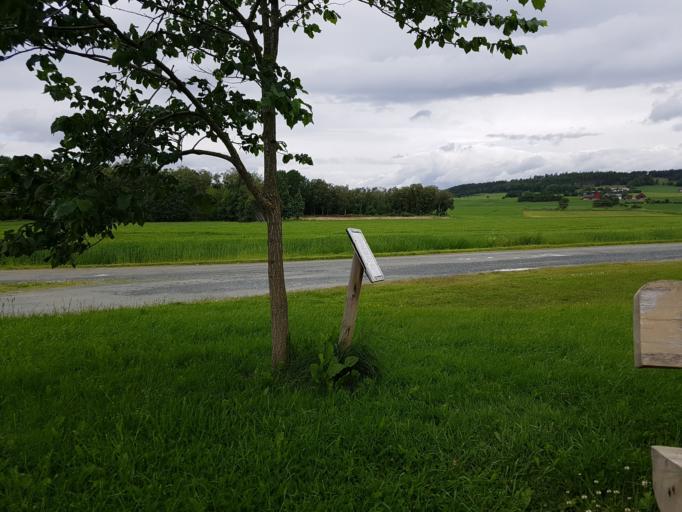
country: NO
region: Nord-Trondelag
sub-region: Frosta
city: Frosta
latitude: 63.5680
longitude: 10.7034
